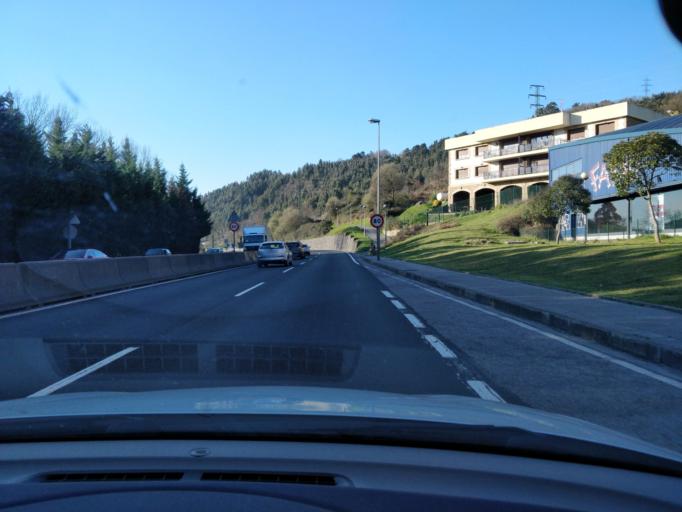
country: ES
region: Basque Country
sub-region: Bizkaia
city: Basauri
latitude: 43.2421
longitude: -2.8755
